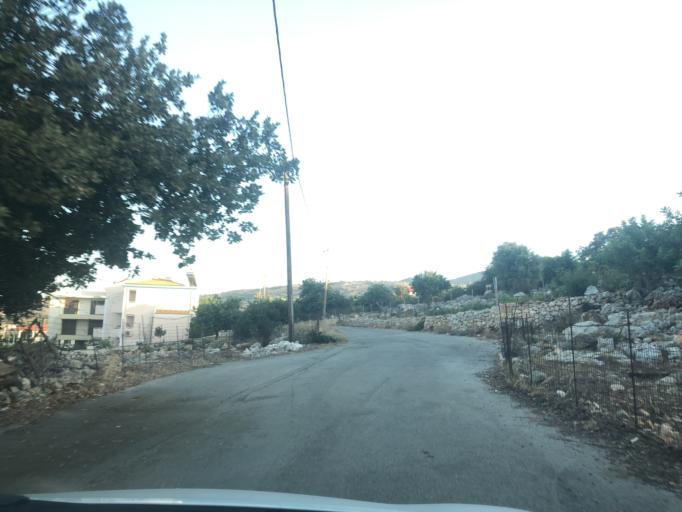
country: GR
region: Crete
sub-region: Nomos Rethymnis
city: Atsipopoulon
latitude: 35.3557
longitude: 24.3973
